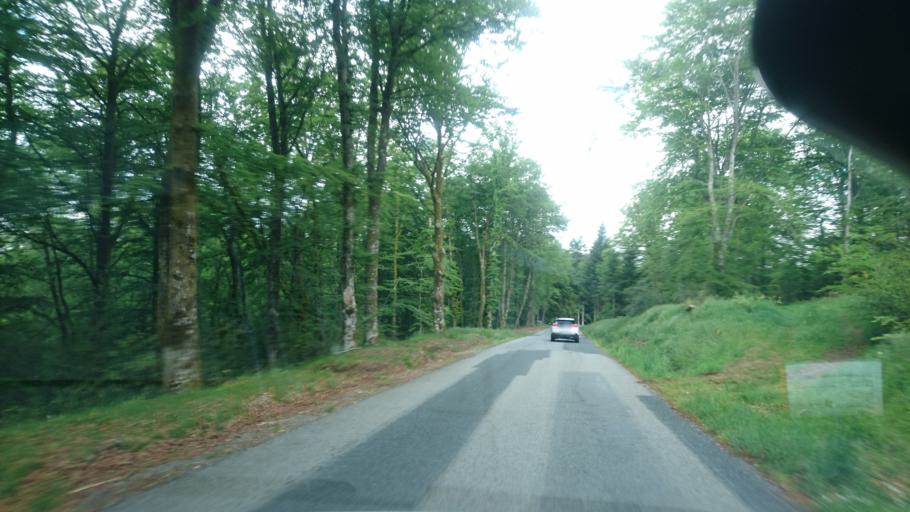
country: FR
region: Limousin
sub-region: Departement de la Haute-Vienne
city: Peyrat-le-Chateau
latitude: 45.7866
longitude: 1.9060
